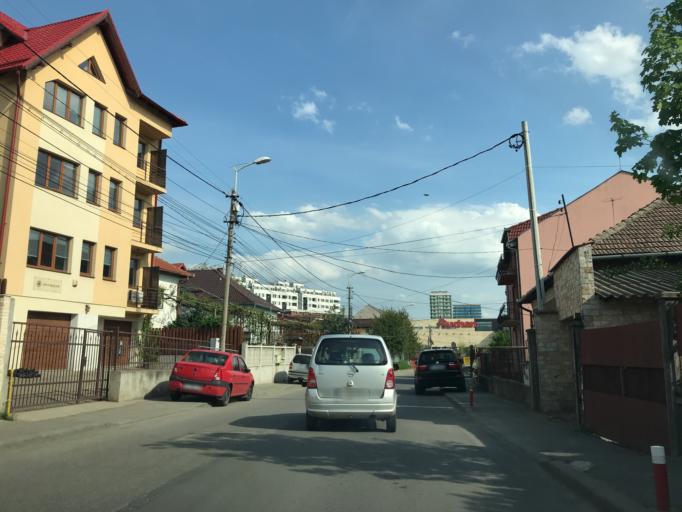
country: RO
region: Cluj
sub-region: Municipiul Cluj-Napoca
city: Cluj-Napoca
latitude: 46.7756
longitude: 23.6255
